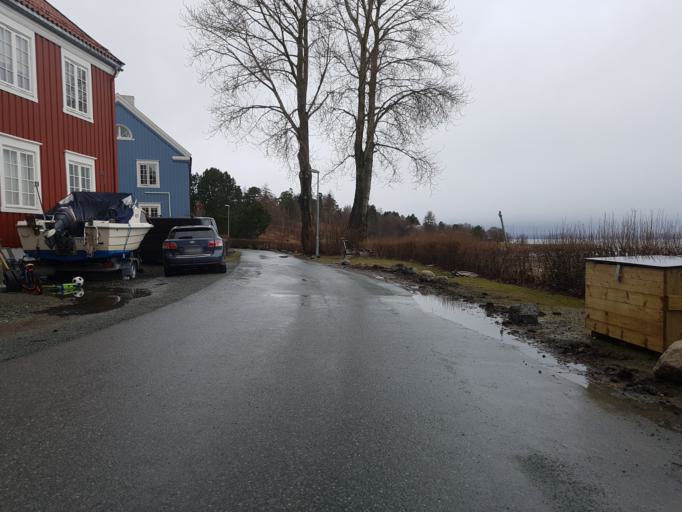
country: NO
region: Sor-Trondelag
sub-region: Trondheim
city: Trondheim
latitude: 63.4383
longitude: 10.4899
